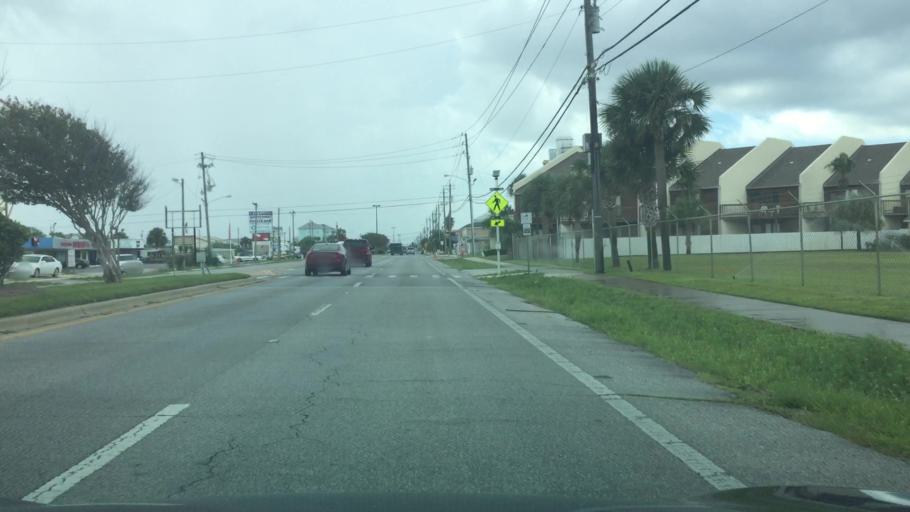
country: US
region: Florida
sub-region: Bay County
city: Lower Grand Lagoon
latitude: 30.1455
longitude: -85.7582
